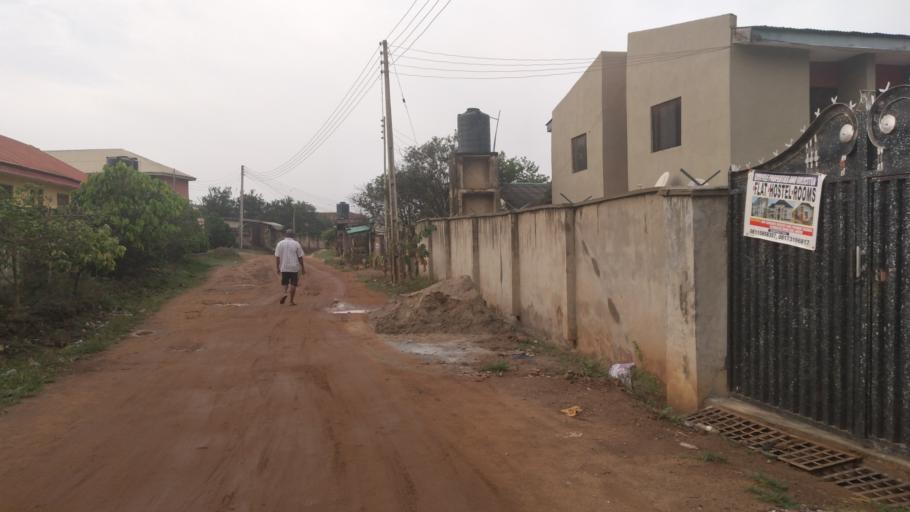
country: NG
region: Ondo
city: Akure
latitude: 7.2960
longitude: 5.1540
